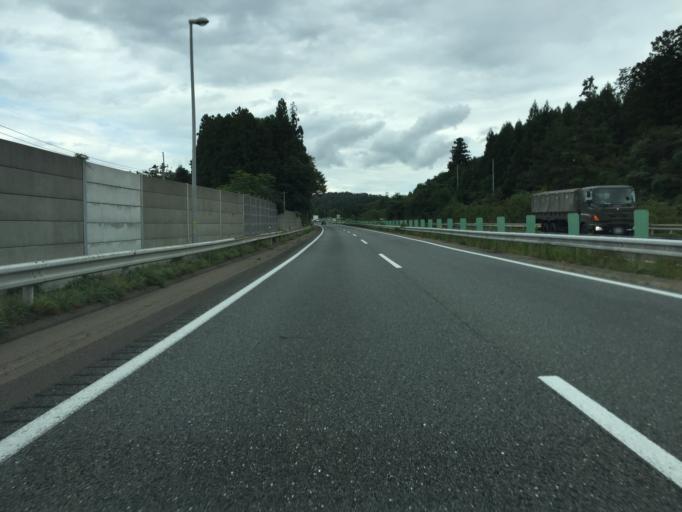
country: JP
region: Miyagi
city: Okawara
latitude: 38.1116
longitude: 140.6964
